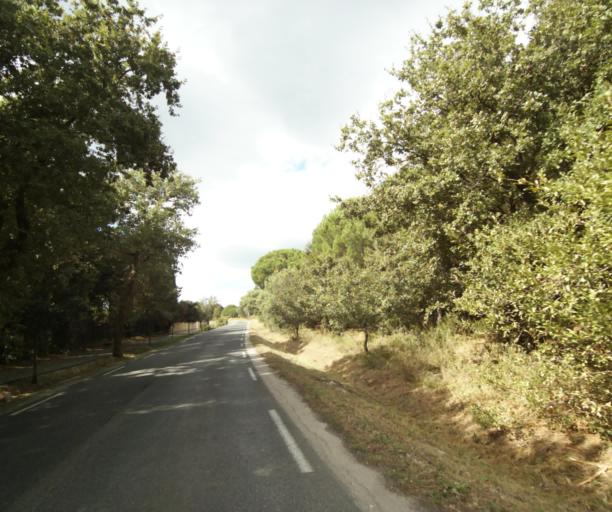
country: FR
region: Languedoc-Roussillon
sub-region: Departement des Pyrenees-Orientales
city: Argelers
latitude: 42.5411
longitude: 3.0404
